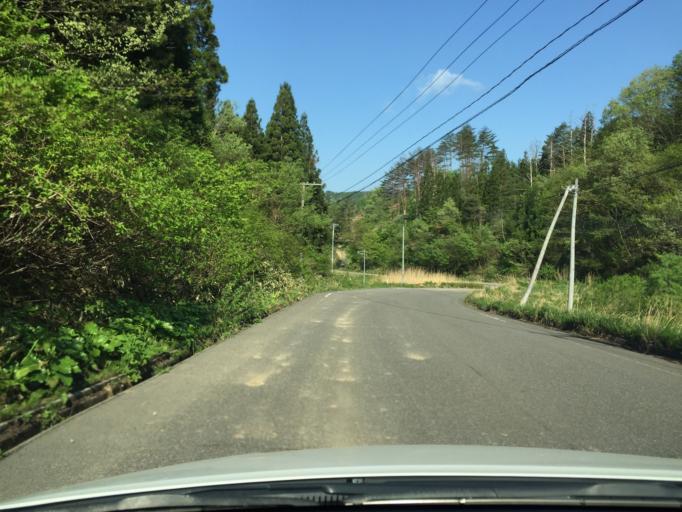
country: JP
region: Fukushima
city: Kitakata
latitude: 37.6734
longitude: 139.6251
